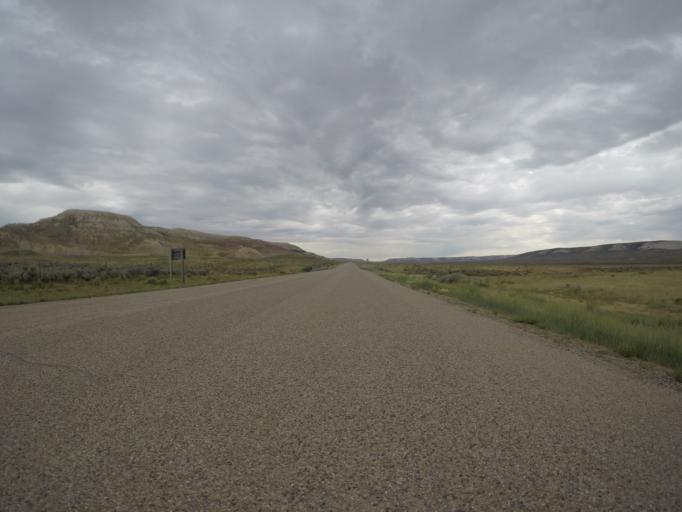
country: US
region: Wyoming
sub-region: Lincoln County
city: Kemmerer
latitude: 41.8230
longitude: -110.7612
